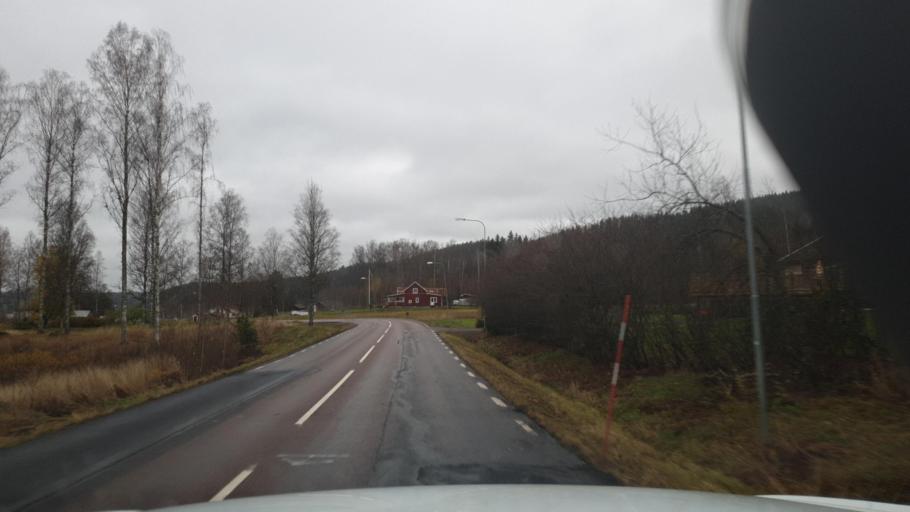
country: SE
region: Vaermland
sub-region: Arvika Kommun
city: Arvika
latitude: 59.8265
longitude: 12.5655
